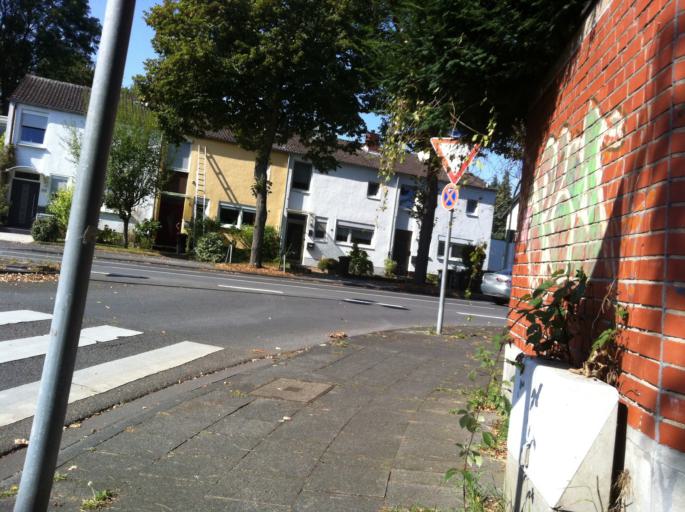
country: DE
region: North Rhine-Westphalia
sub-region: Regierungsbezirk Koln
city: Hoehenberg
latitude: 50.9251
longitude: 7.0231
